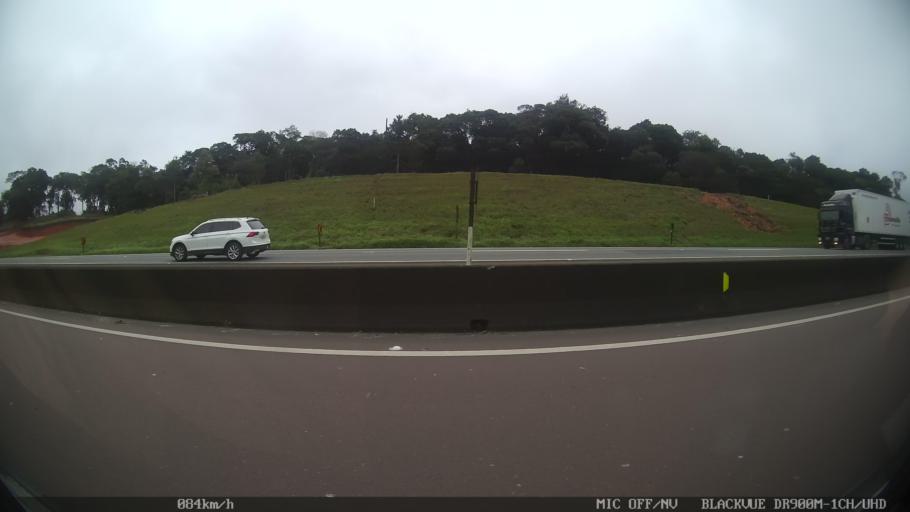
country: BR
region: Parana
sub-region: Sao Jose Dos Pinhais
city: Sao Jose dos Pinhais
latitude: -25.8002
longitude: -49.1332
